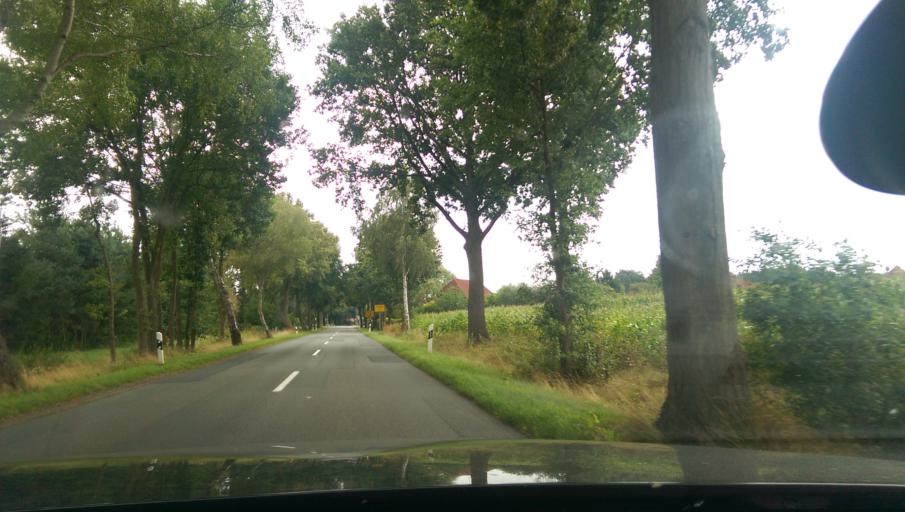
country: DE
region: Lower Saxony
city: Frankenfeld
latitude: 52.6993
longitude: 9.4788
